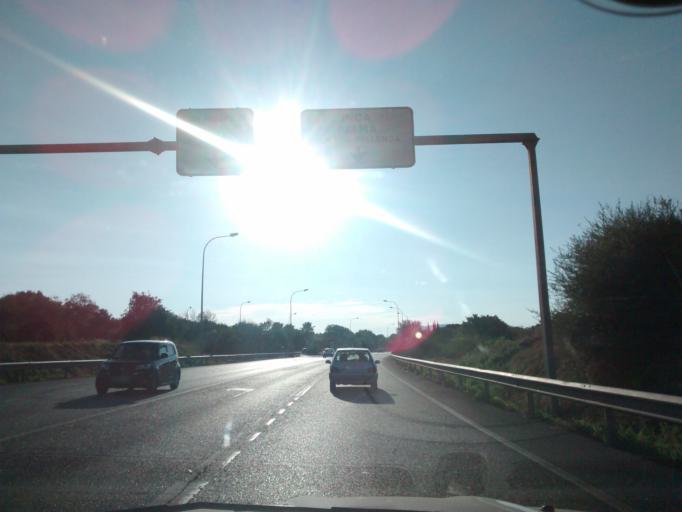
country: ES
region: Balearic Islands
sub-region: Illes Balears
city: Alcudia
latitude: 39.8423
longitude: 3.1000
